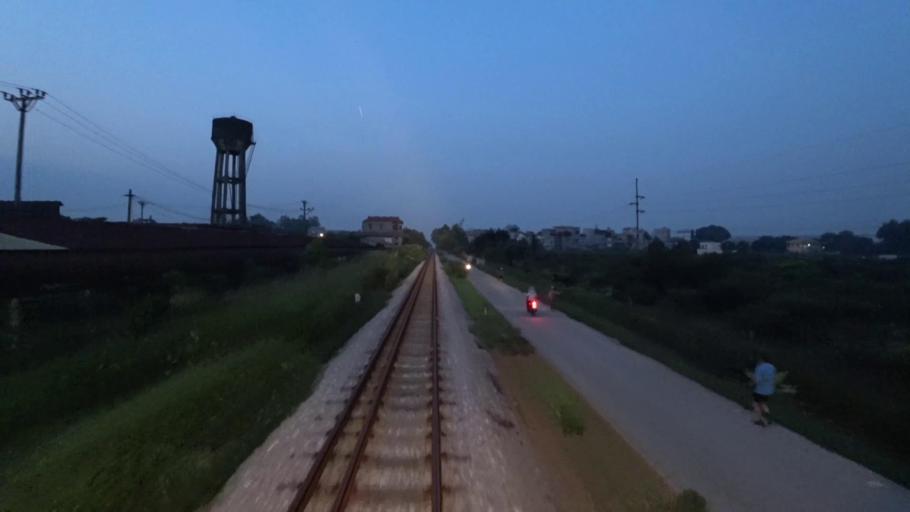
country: VN
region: Ha Noi
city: Soc Son
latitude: 21.2572
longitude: 105.8619
